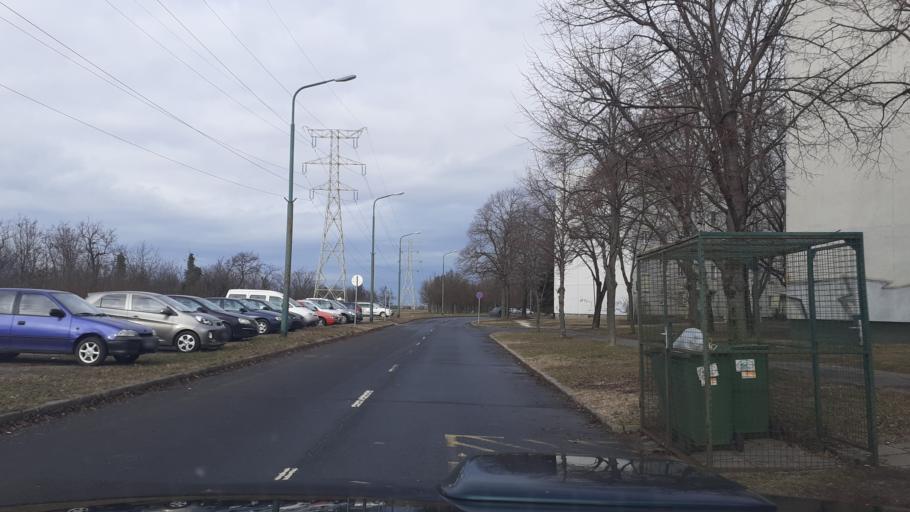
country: HU
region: Fejer
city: dunaujvaros
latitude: 46.9684
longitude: 18.9272
